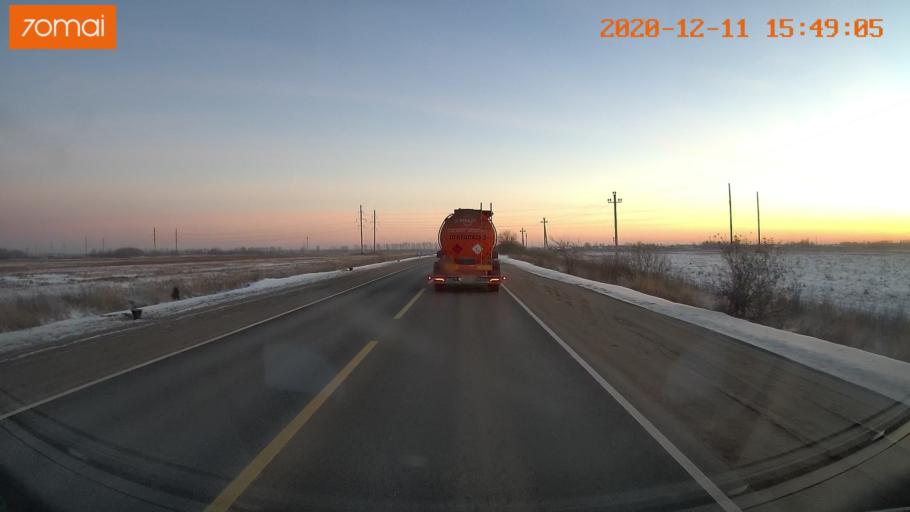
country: RU
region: Ivanovo
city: Novo-Talitsy
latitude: 56.9902
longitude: 40.8718
